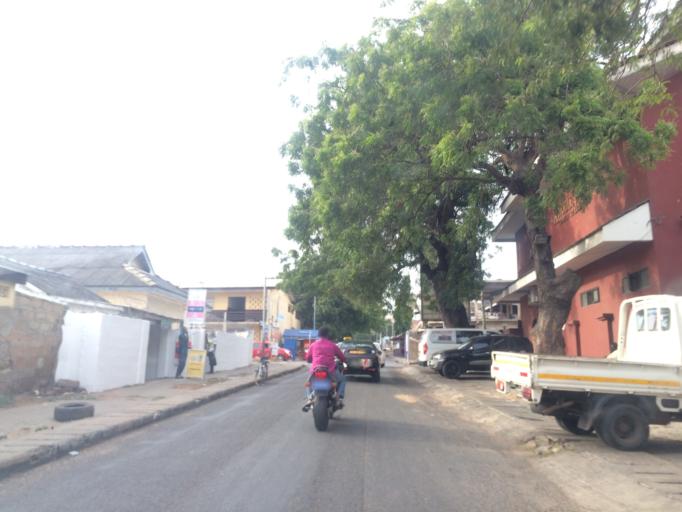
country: GH
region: Greater Accra
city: Accra
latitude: 5.5555
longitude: -0.1852
